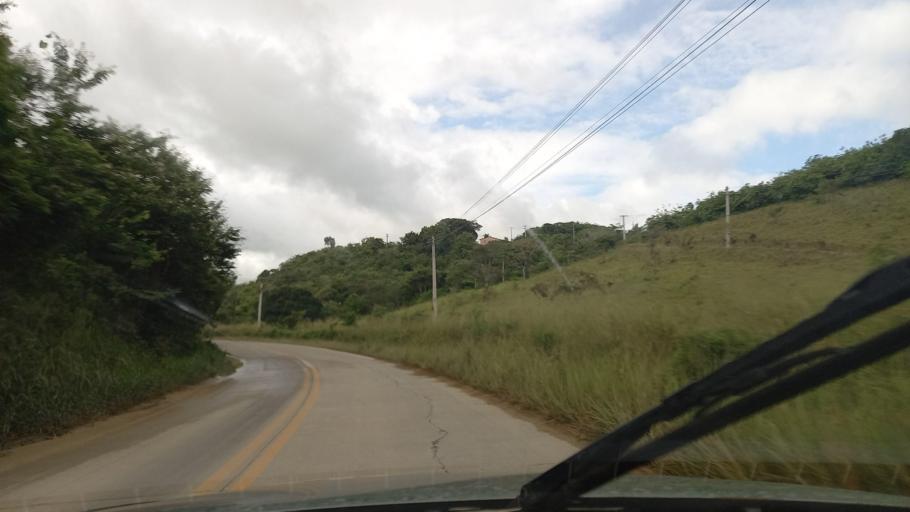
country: BR
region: Pernambuco
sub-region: Quipapa
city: Quipapa
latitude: -8.7909
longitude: -35.9802
